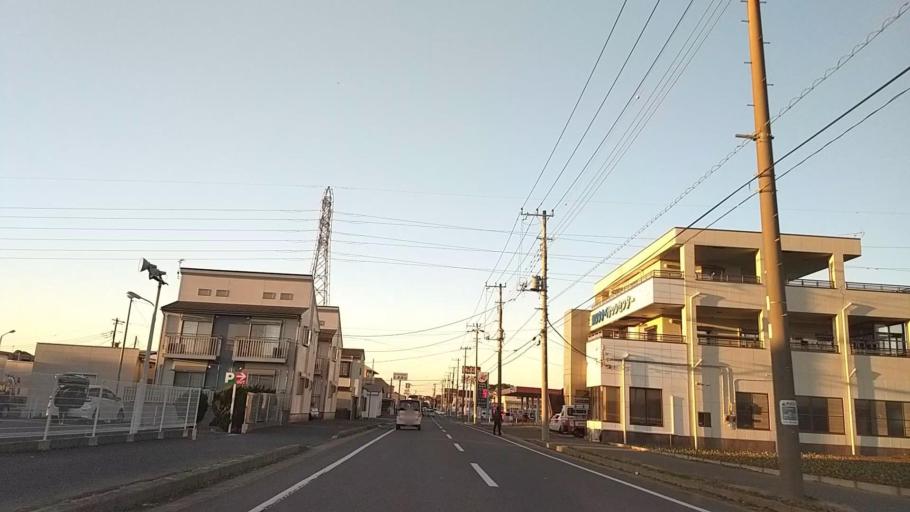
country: JP
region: Chiba
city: Hasaki
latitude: 35.7185
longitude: 140.8367
